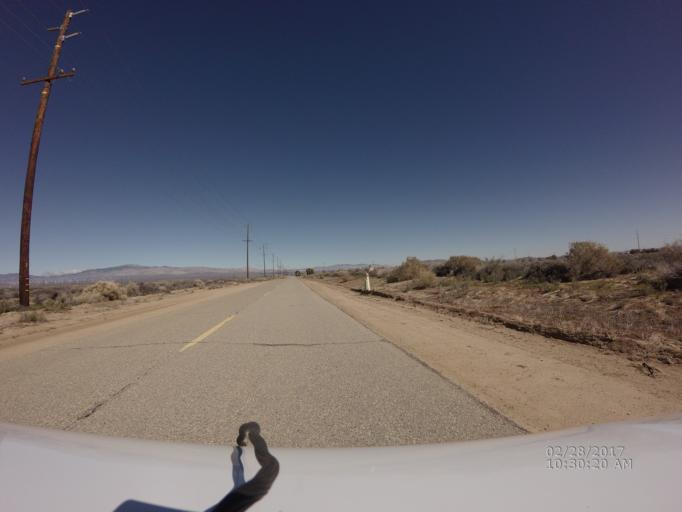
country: US
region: California
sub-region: Kern County
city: Rosamond
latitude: 34.8022
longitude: -118.3259
